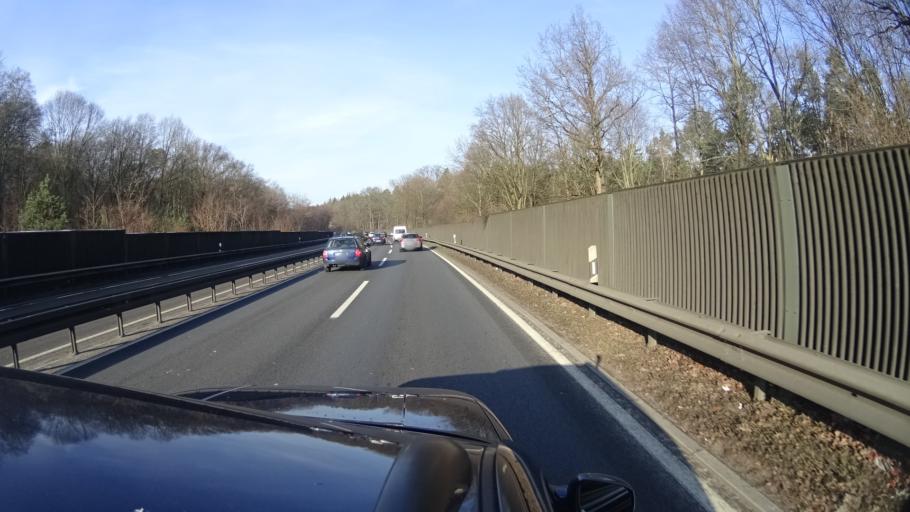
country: DE
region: Berlin
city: Tegel
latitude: 52.6006
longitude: 13.2808
